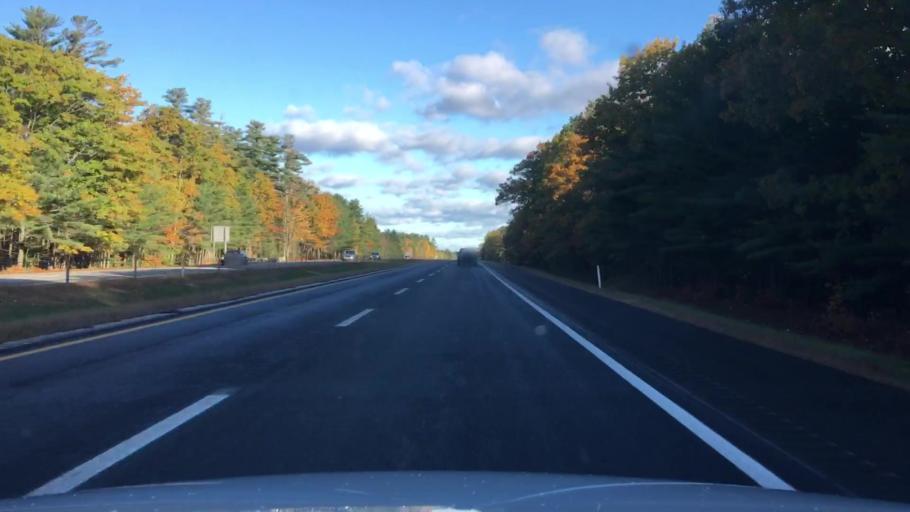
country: US
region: Maine
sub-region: Penobscot County
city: Orono
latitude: 44.9120
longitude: -68.6966
